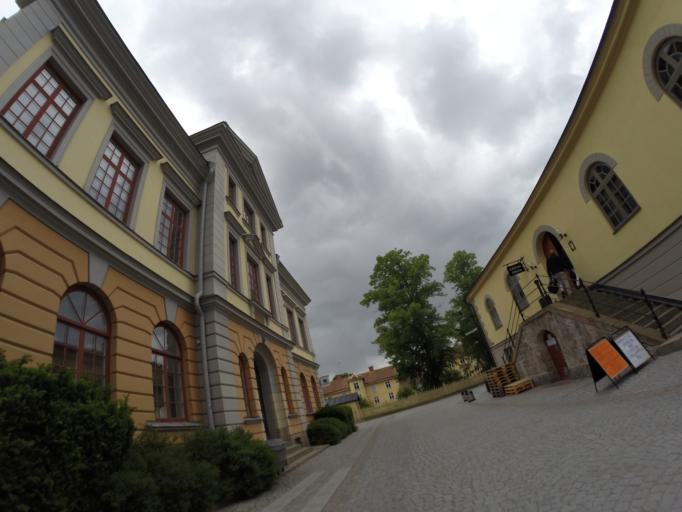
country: SE
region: Soedermanland
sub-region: Eskilstuna Kommun
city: Eskilstuna
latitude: 59.3754
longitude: 16.5086
